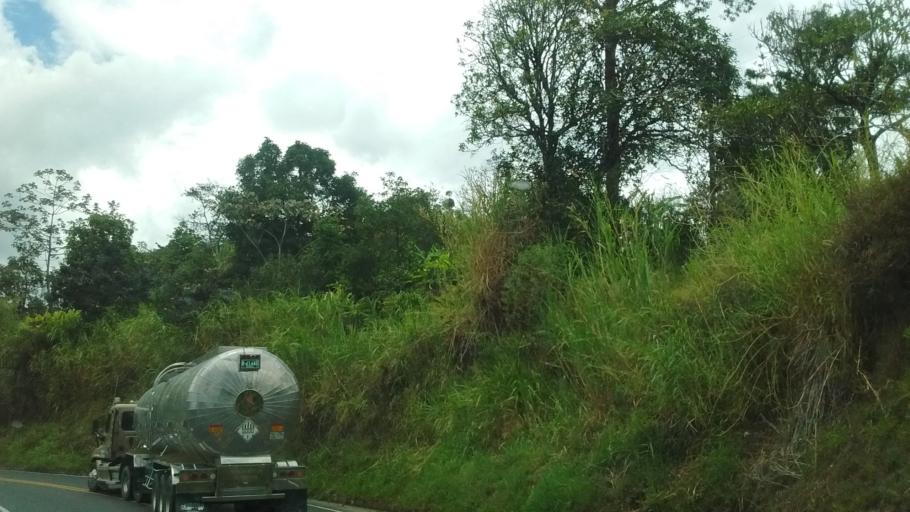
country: CO
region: Cauca
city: Rosas
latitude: 2.3152
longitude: -76.6879
